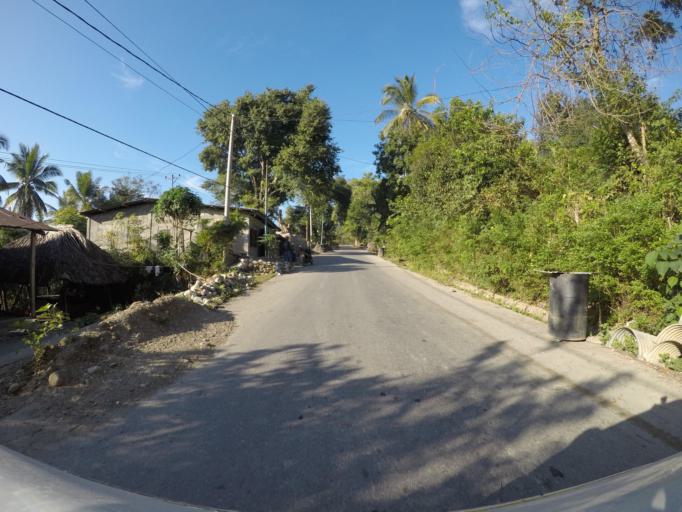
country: TL
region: Viqueque
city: Viqueque
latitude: -8.8693
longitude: 126.3620
